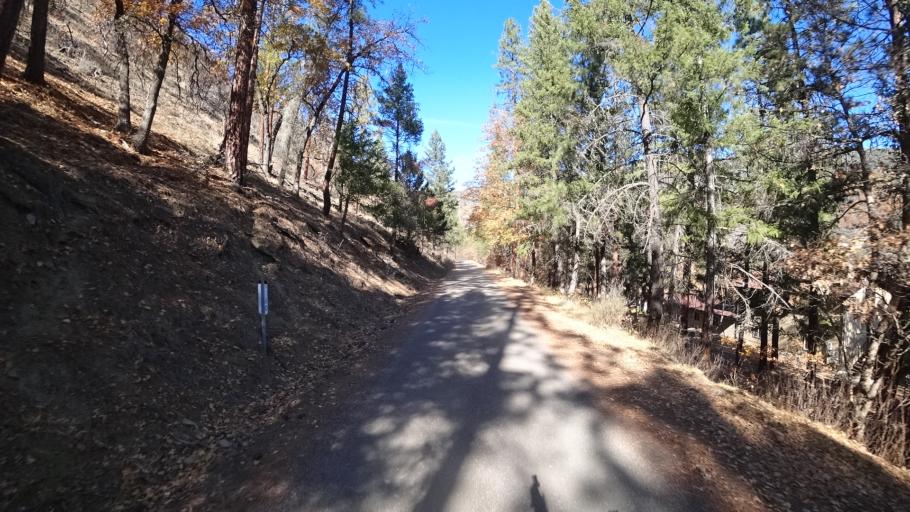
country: US
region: California
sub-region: Siskiyou County
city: Yreka
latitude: 41.8609
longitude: -122.7068
